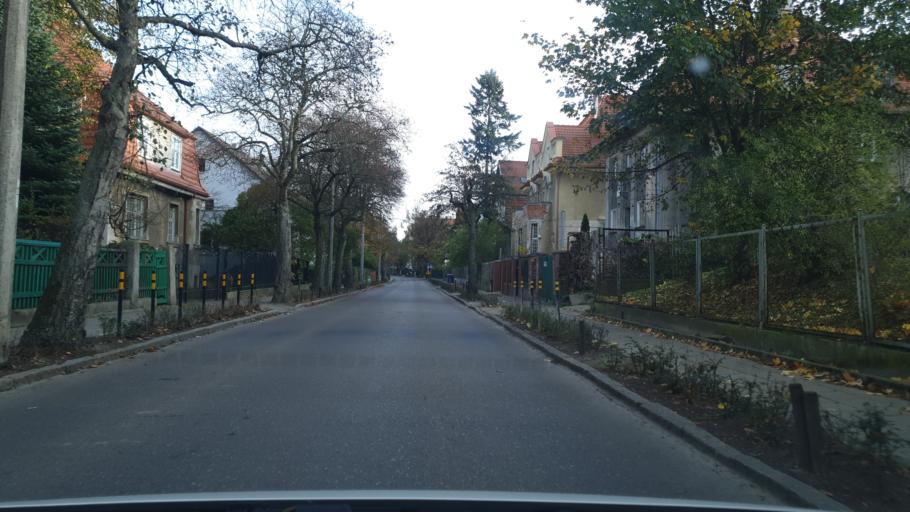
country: PL
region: Pomeranian Voivodeship
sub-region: Gdansk
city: Gdansk
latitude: 54.3769
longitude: 18.6012
